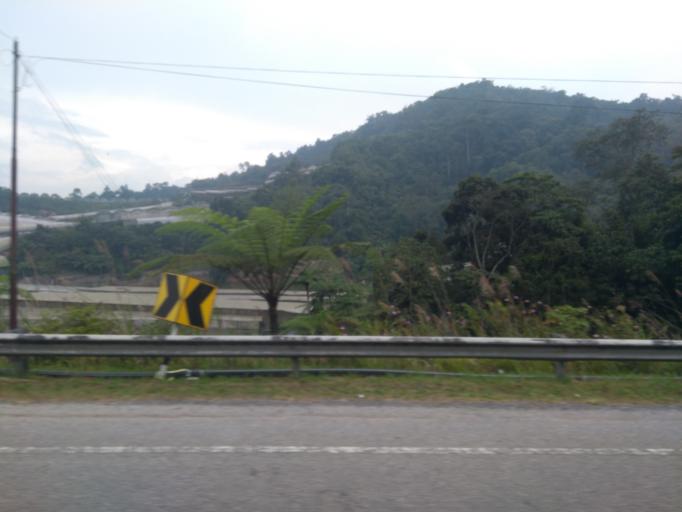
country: MY
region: Pahang
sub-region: Cameron Highlands
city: Tanah Rata
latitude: 4.5768
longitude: 101.3824
